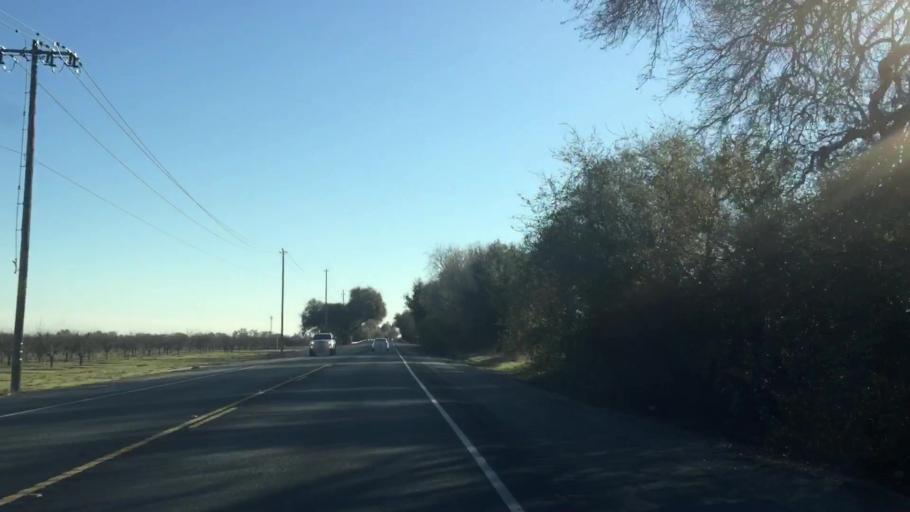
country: US
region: California
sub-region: Sutter County
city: Live Oak
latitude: 39.3193
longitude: -121.5961
